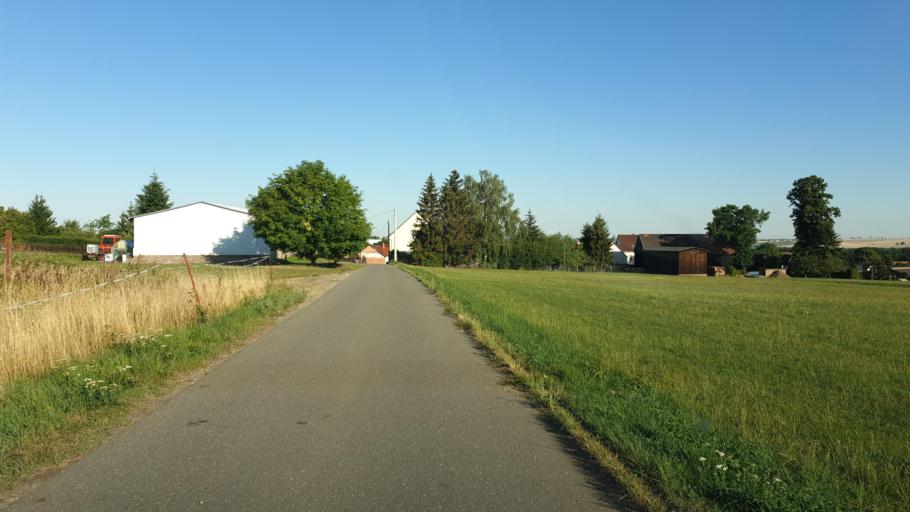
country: DE
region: Saxony
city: Lichtentanne
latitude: 50.6738
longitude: 12.4362
